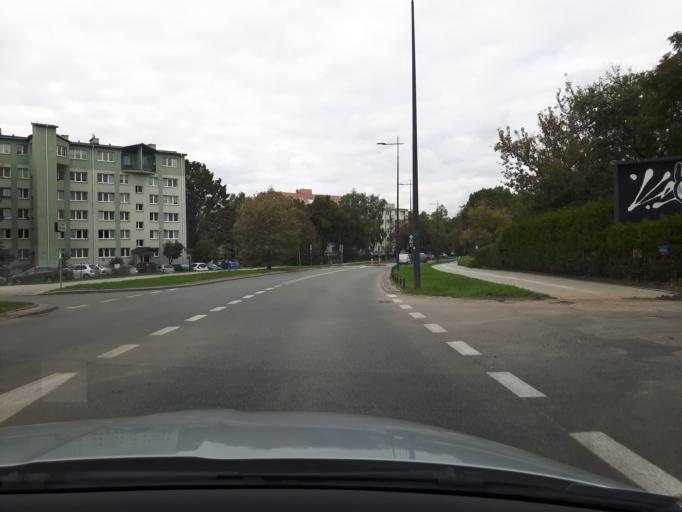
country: PL
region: Masovian Voivodeship
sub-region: Warszawa
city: Mokotow
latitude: 52.1748
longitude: 21.0102
